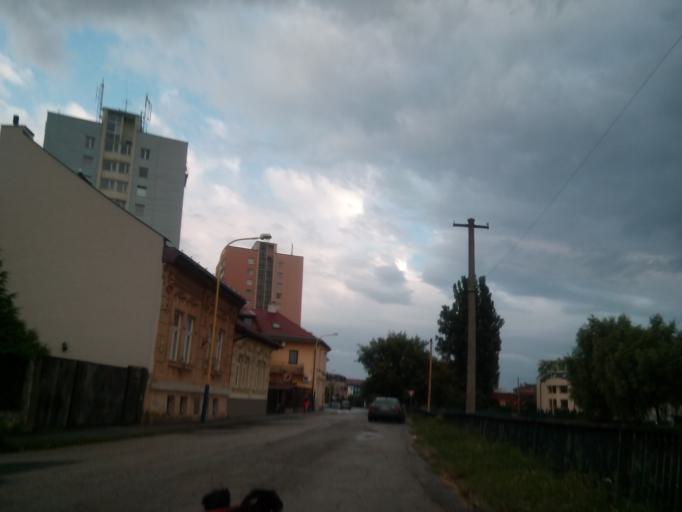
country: SK
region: Kosicky
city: Kosice
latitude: 48.7331
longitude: 21.2560
